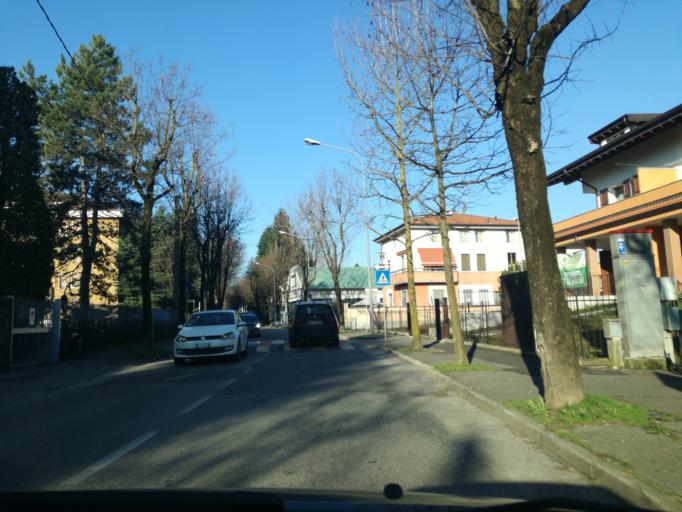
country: IT
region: Lombardy
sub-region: Provincia di Monza e Brianza
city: Vimercate
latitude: 45.6204
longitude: 9.3736
